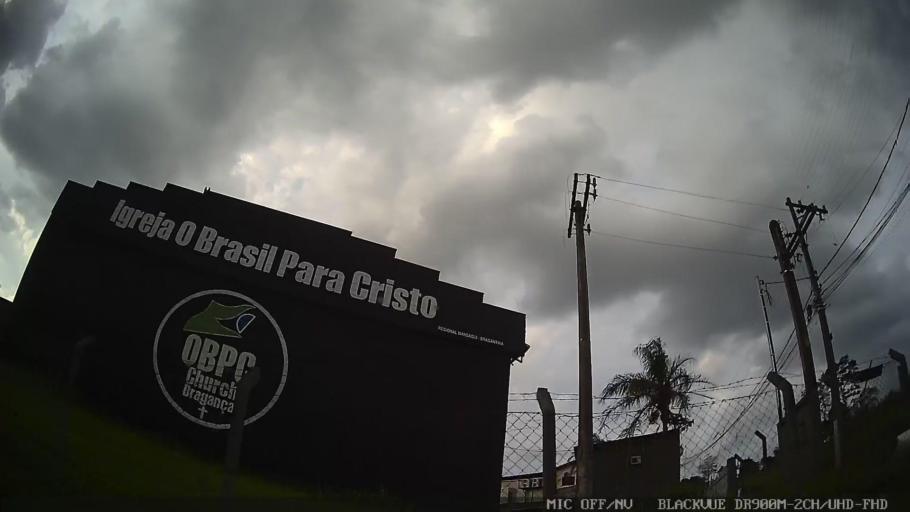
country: BR
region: Sao Paulo
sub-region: Braganca Paulista
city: Braganca Paulista
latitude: -22.9301
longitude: -46.5306
